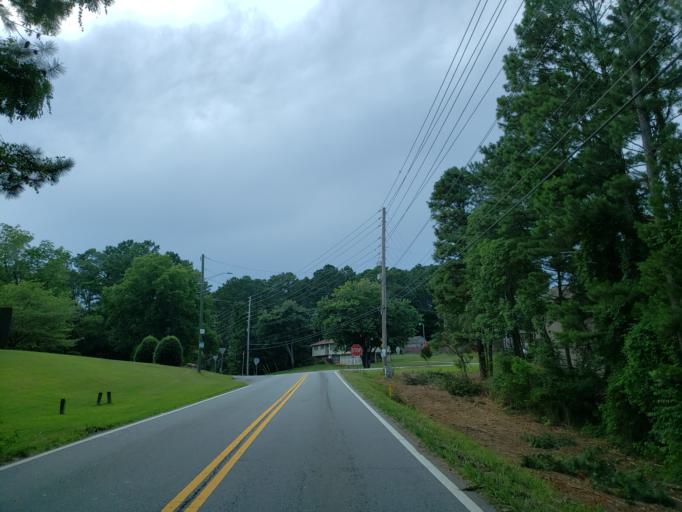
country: US
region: Georgia
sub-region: Cherokee County
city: Holly Springs
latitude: 34.1254
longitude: -84.4095
